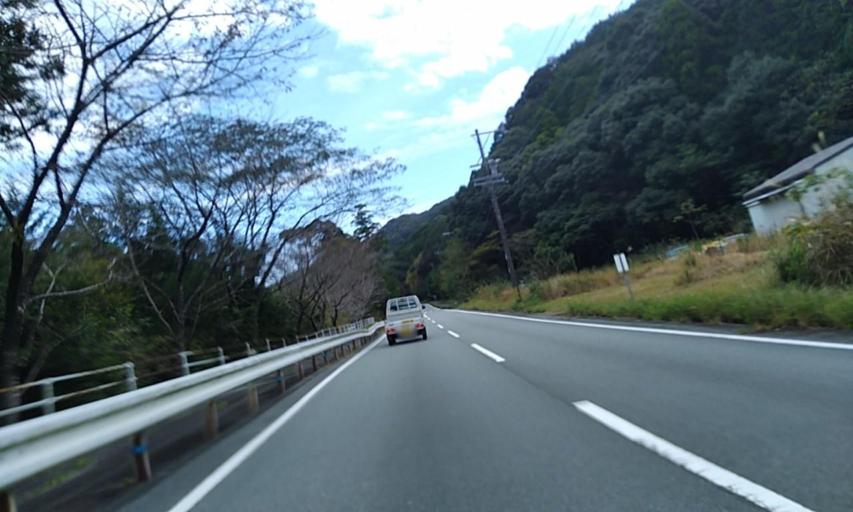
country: JP
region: Mie
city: Ise
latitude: 34.3011
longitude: 136.6066
